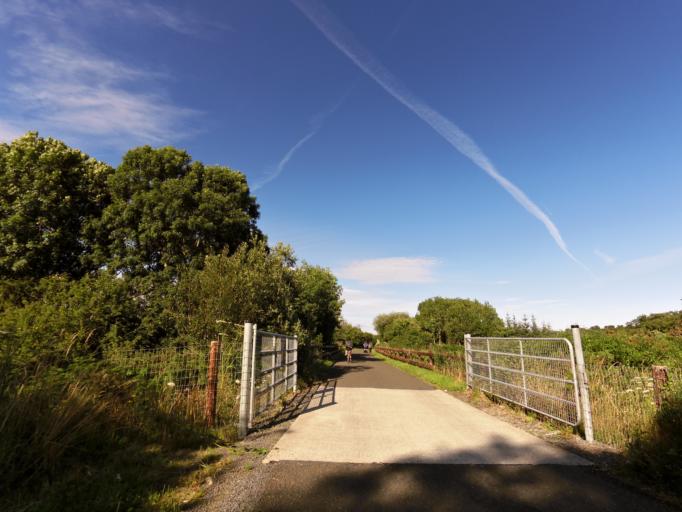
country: IE
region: Leinster
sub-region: Kilkenny
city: Mooncoin
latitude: 52.2451
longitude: -7.2600
